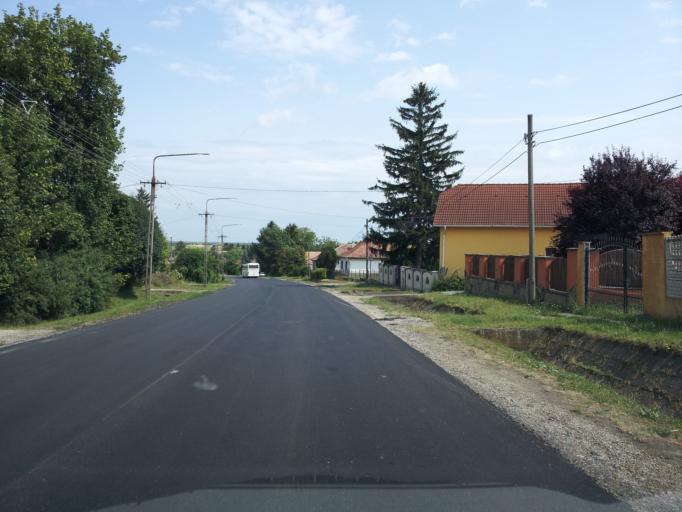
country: HU
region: Fejer
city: Enying
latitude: 46.9541
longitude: 18.2208
